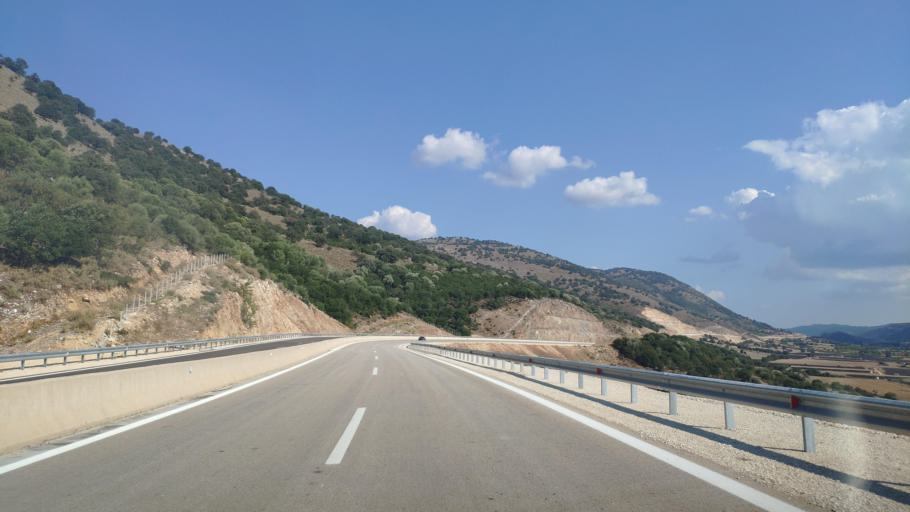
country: GR
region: West Greece
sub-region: Nomos Aitolias kai Akarnanias
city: Katouna
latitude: 38.8383
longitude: 21.1123
